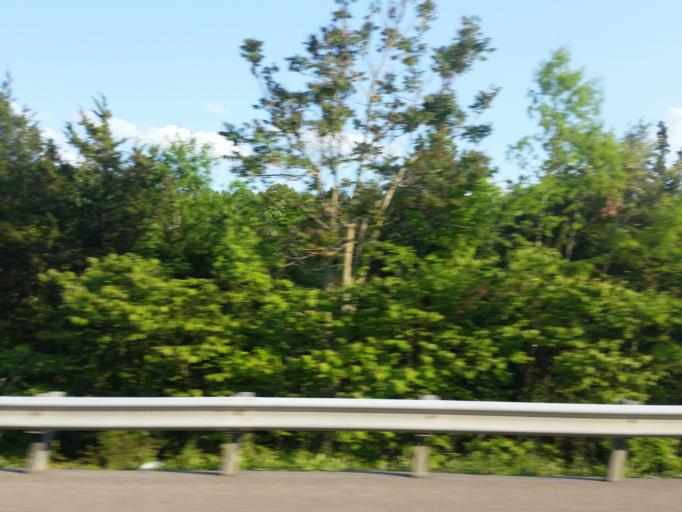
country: US
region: Virginia
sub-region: Tazewell County
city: Raven
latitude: 36.9990
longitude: -81.8239
